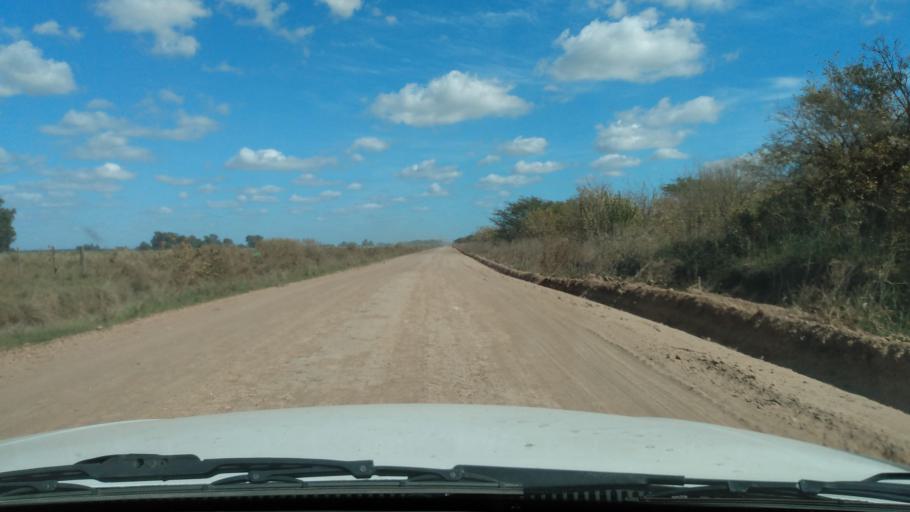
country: AR
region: Buenos Aires
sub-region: Partido de Navarro
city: Navarro
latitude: -35.0250
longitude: -59.4391
